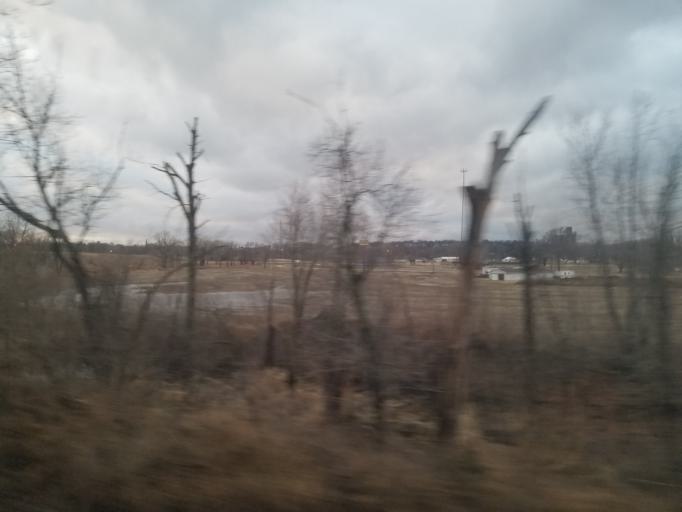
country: US
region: Iowa
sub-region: Des Moines County
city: Burlington
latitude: 40.8344
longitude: -91.0249
